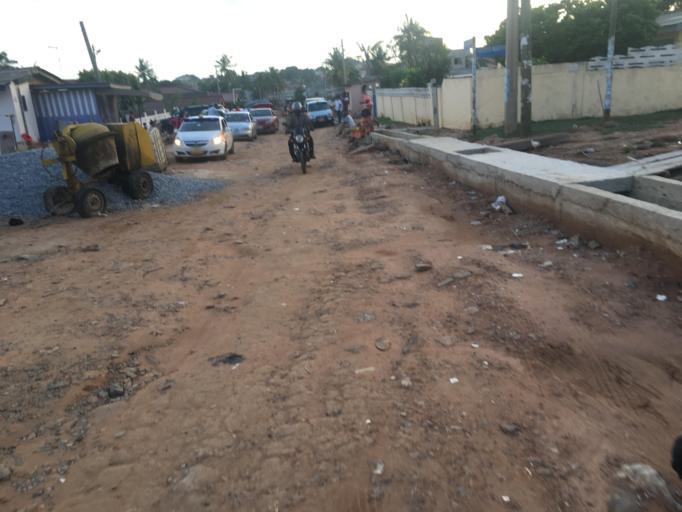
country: GH
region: Greater Accra
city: Accra
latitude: 5.5686
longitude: -0.2525
